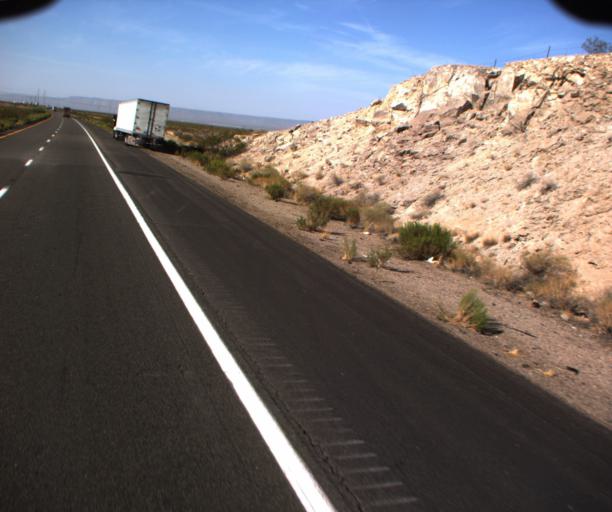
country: US
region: Arizona
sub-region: Mohave County
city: Kingman
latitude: 35.1170
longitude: -114.1139
